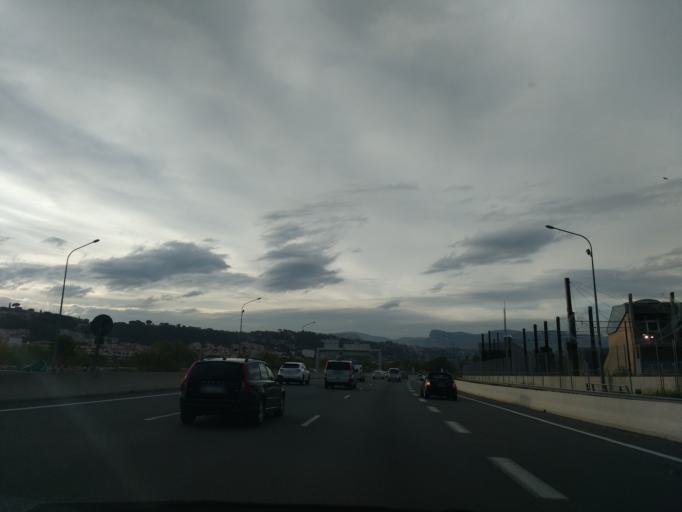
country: FR
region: Provence-Alpes-Cote d'Azur
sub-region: Departement des Alpes-Maritimes
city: Saint-Laurent-du-Var
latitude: 43.6759
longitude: 7.1962
